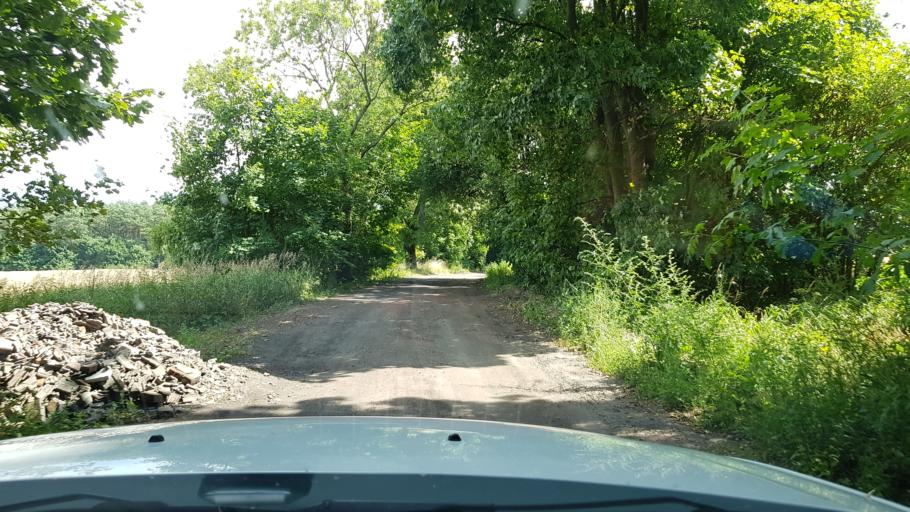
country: PL
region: West Pomeranian Voivodeship
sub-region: Powiat walecki
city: Walcz
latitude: 53.2561
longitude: 16.5050
